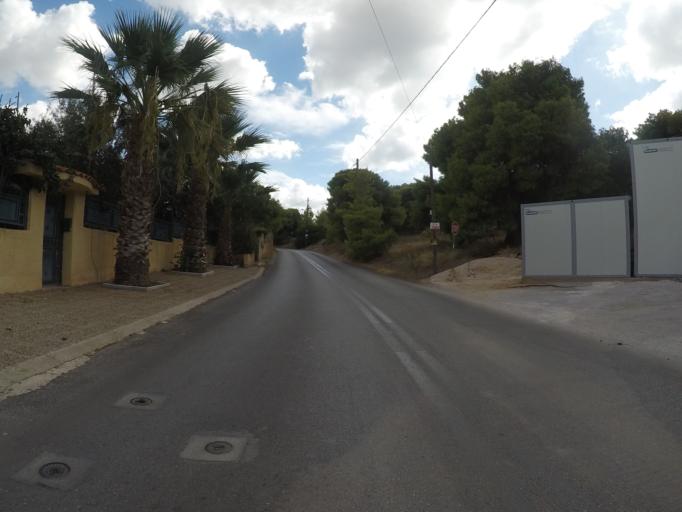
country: GR
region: Attica
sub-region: Nomarchia Anatolikis Attikis
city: Agios Dimitrios Kropias
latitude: 37.8169
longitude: 23.8640
